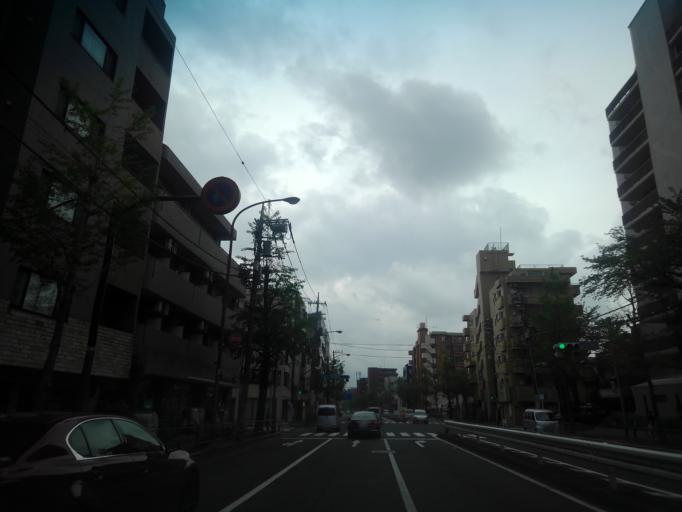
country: JP
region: Tokyo
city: Musashino
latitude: 35.7231
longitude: 139.5726
